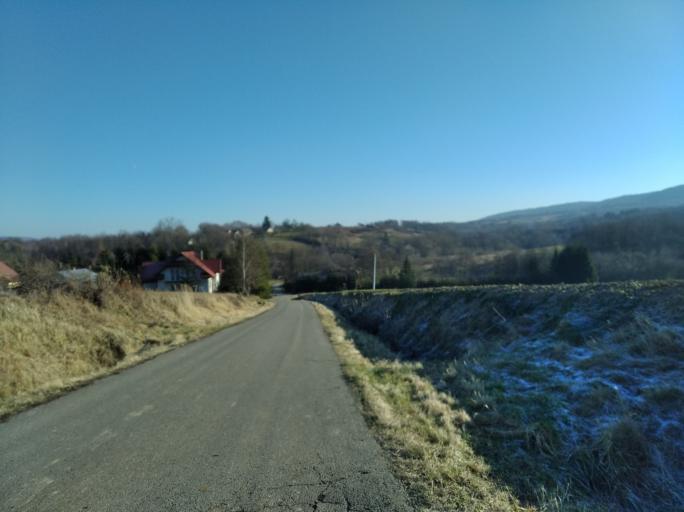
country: PL
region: Subcarpathian Voivodeship
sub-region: Powiat strzyzowski
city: Wysoka Strzyzowska
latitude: 49.8509
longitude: 21.7568
